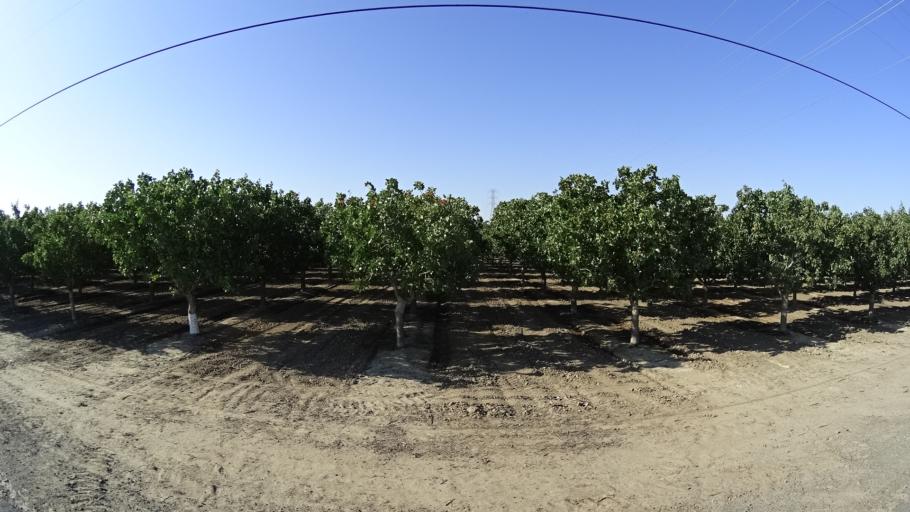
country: US
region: California
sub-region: Fresno County
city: Riverdale
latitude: 36.3766
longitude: -119.8893
